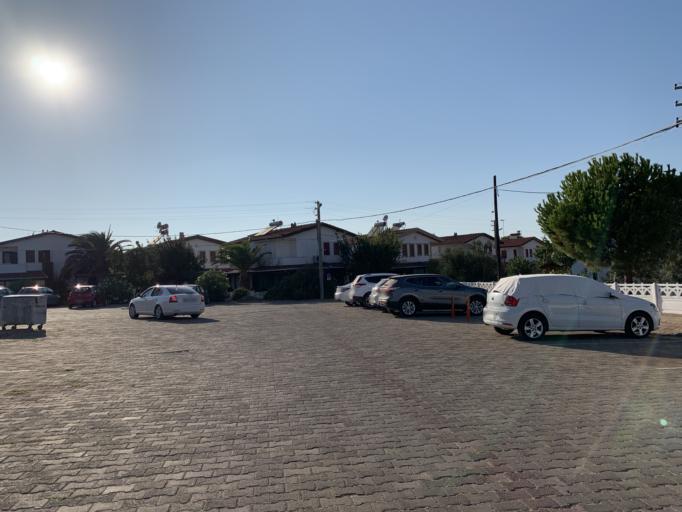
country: TR
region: Balikesir
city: Ayvalik
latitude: 39.3517
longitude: 26.6494
